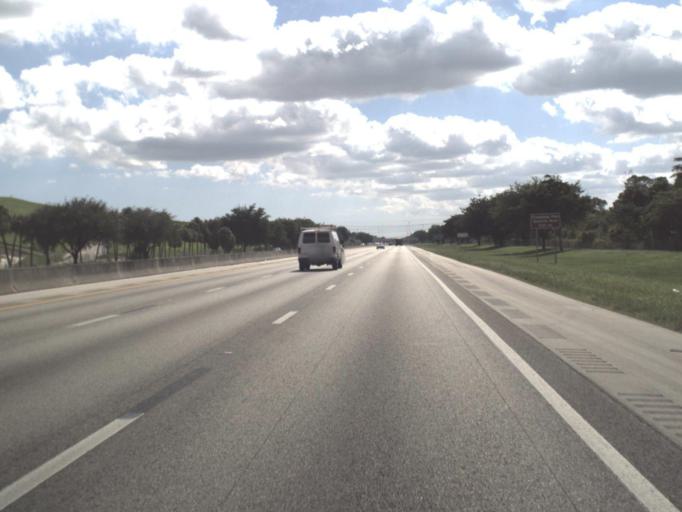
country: US
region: Florida
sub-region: Broward County
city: Coconut Creek
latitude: 26.2877
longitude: -80.1692
